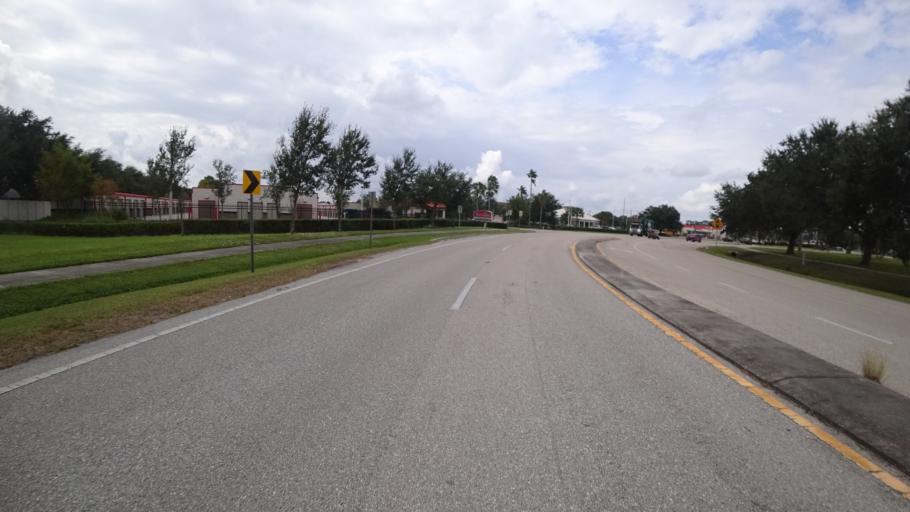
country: US
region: Florida
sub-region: Manatee County
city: Ellenton
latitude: 27.5416
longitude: -82.4762
